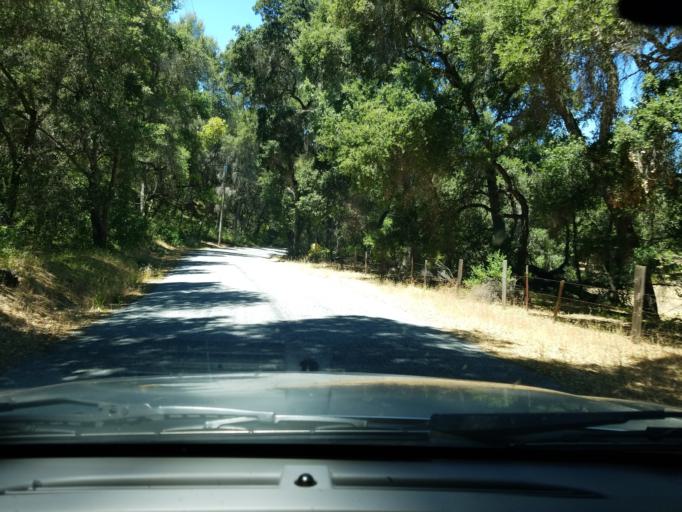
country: US
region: California
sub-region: Monterey County
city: Gonzales
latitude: 36.3792
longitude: -121.5700
